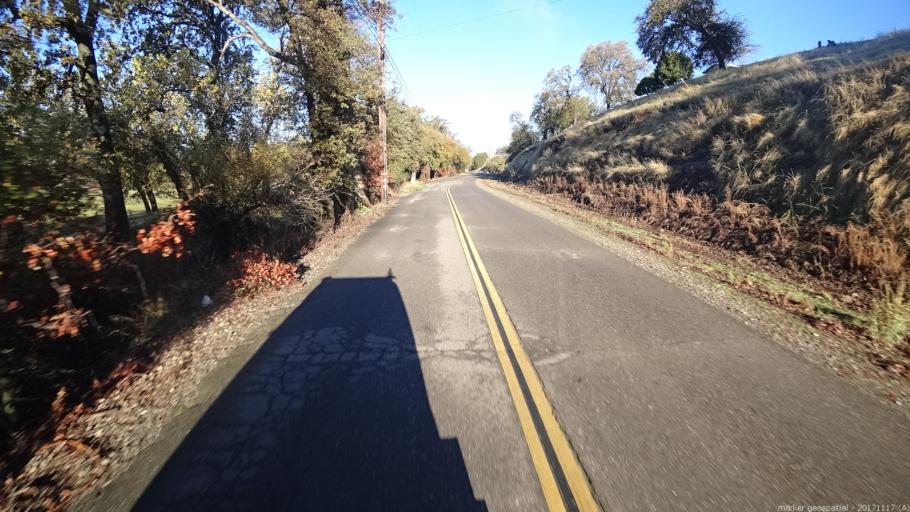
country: US
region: California
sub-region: Shasta County
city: Cottonwood
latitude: 40.4136
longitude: -122.1903
